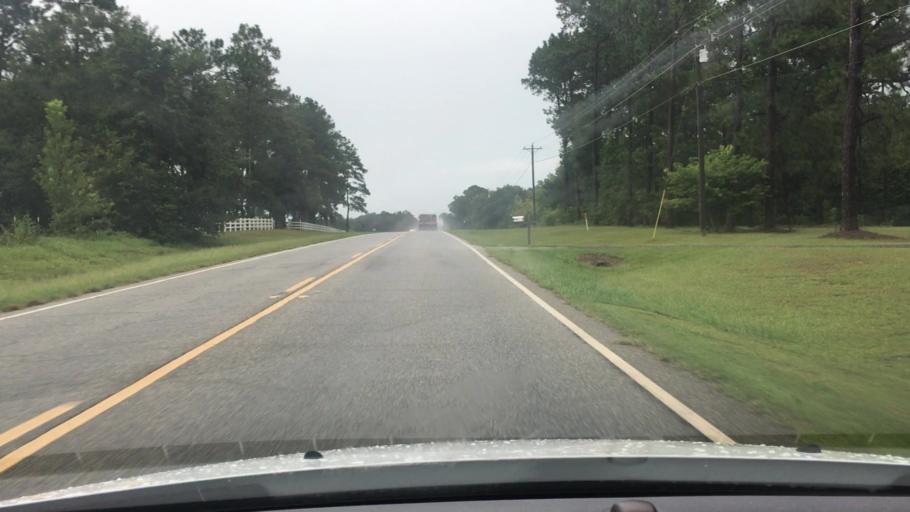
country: US
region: Georgia
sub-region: Grady County
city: Cairo
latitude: 30.7972
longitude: -84.2610
